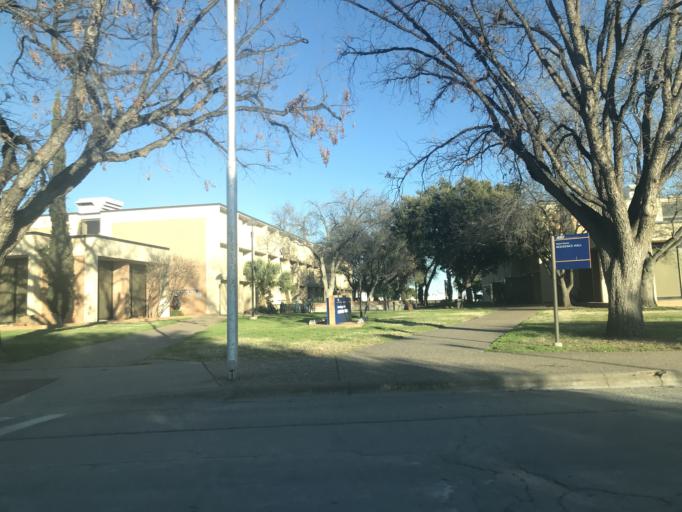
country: US
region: Texas
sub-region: Tom Green County
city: San Angelo
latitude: 31.4399
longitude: -100.4574
